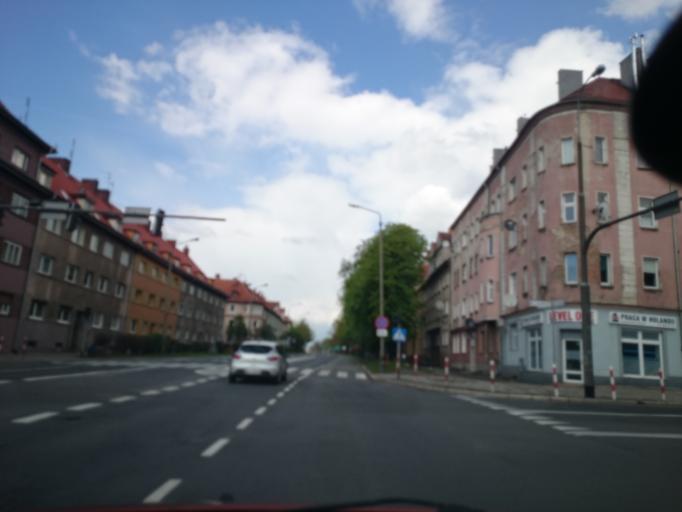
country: PL
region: Opole Voivodeship
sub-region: Powiat opolski
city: Opole
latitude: 50.6639
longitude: 17.9425
